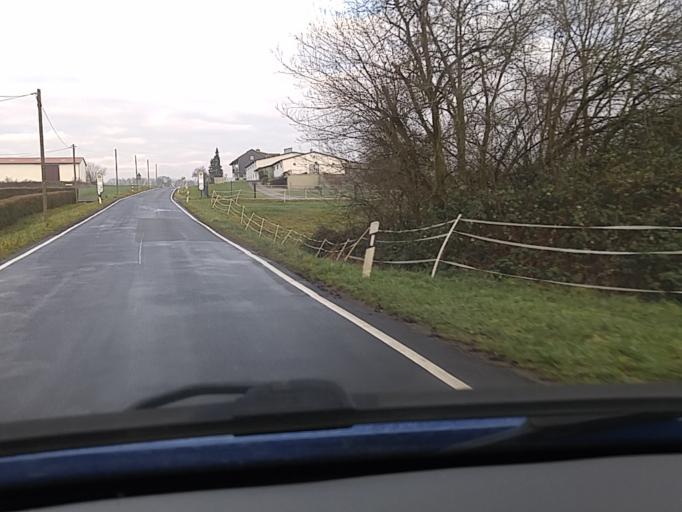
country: DE
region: Hesse
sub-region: Regierungsbezirk Darmstadt
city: Friedberg
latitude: 50.3581
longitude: 8.7677
